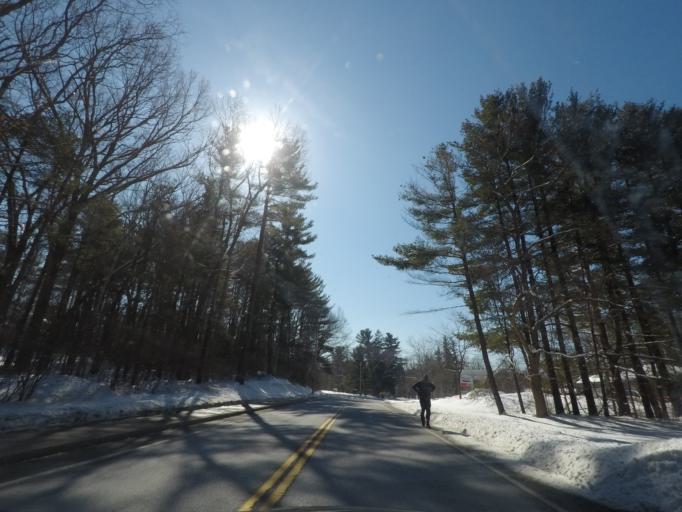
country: US
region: New York
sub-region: Saratoga County
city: Country Knolls
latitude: 42.9118
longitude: -73.8218
